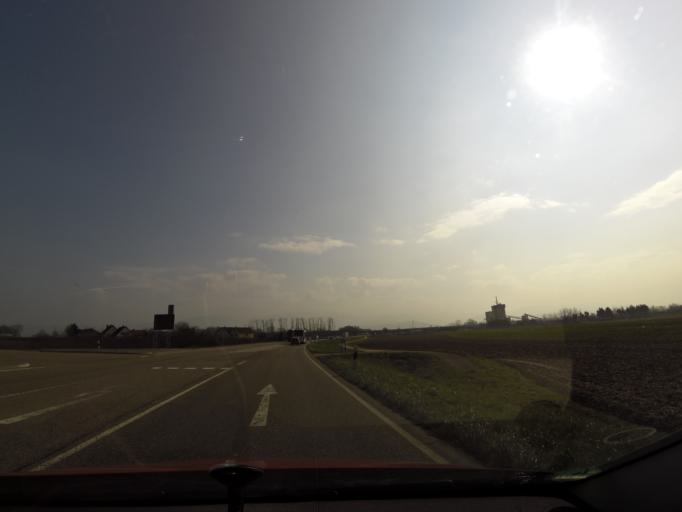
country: DE
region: Baden-Wuerttemberg
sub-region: Freiburg Region
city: Achern
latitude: 48.6459
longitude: 8.0229
